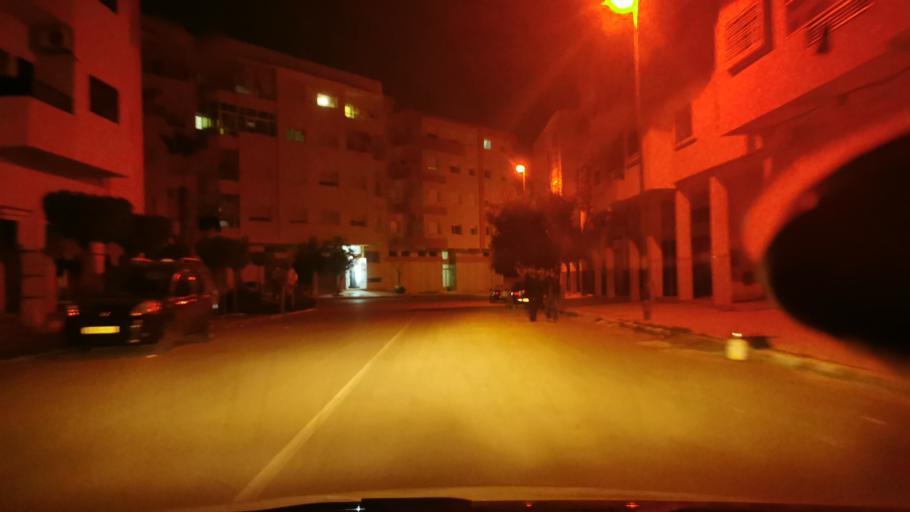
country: MA
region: Fes-Boulemane
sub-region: Fes
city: Fes
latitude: 34.0101
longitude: -4.9688
